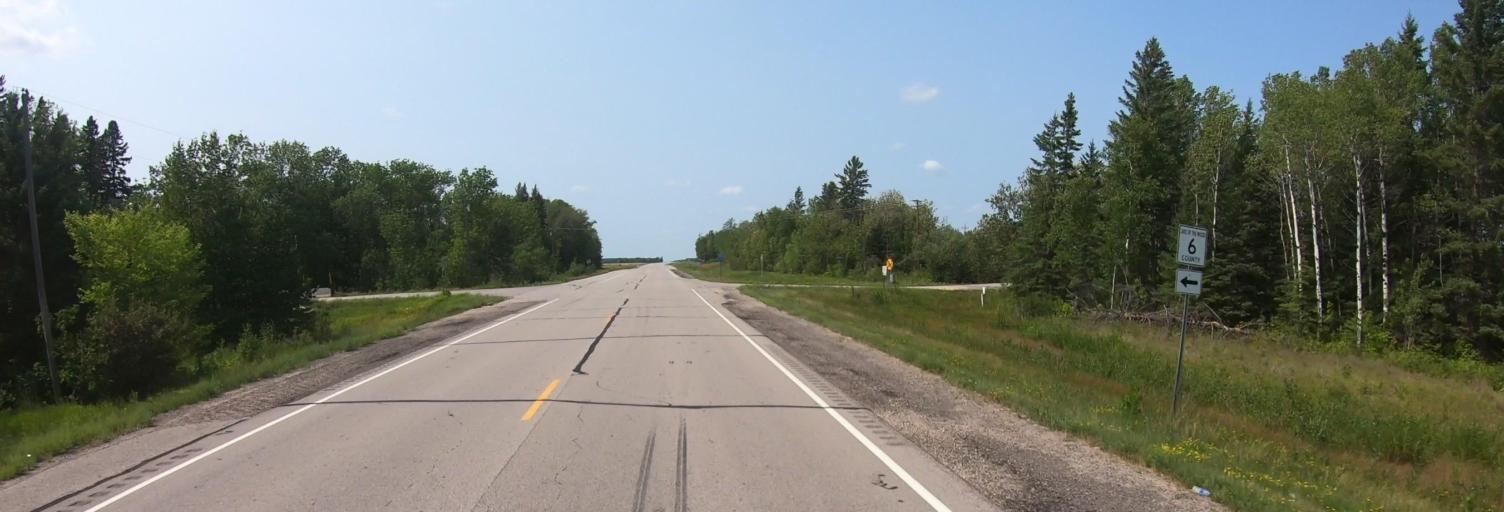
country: US
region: Minnesota
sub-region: Lake of the Woods County
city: Baudette
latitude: 48.7162
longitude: -94.7354
